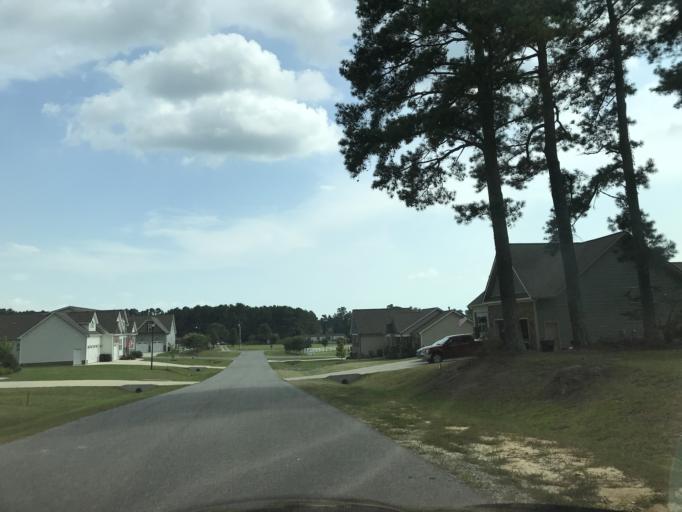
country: US
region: North Carolina
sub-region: Johnston County
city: Four Oaks
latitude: 35.5168
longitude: -78.5316
